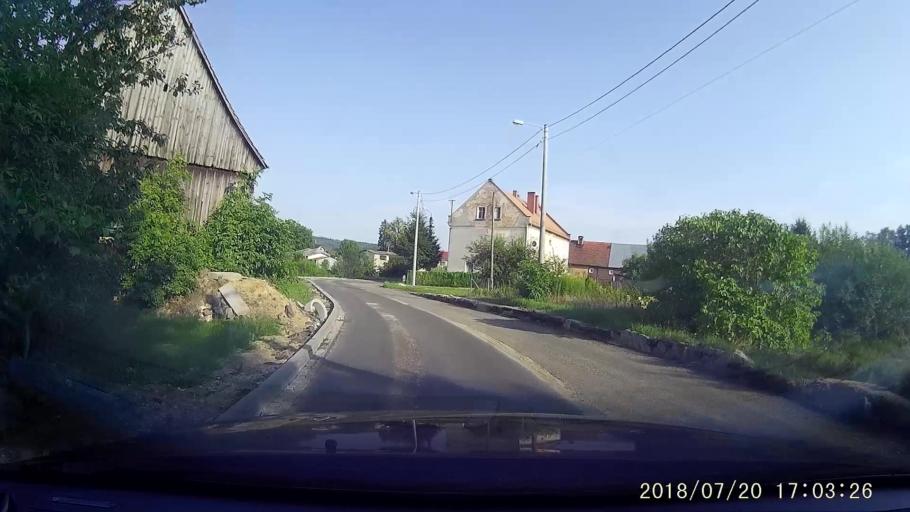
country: PL
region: Lower Silesian Voivodeship
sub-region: Powiat lubanski
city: Lesna
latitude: 51.0281
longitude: 15.2601
